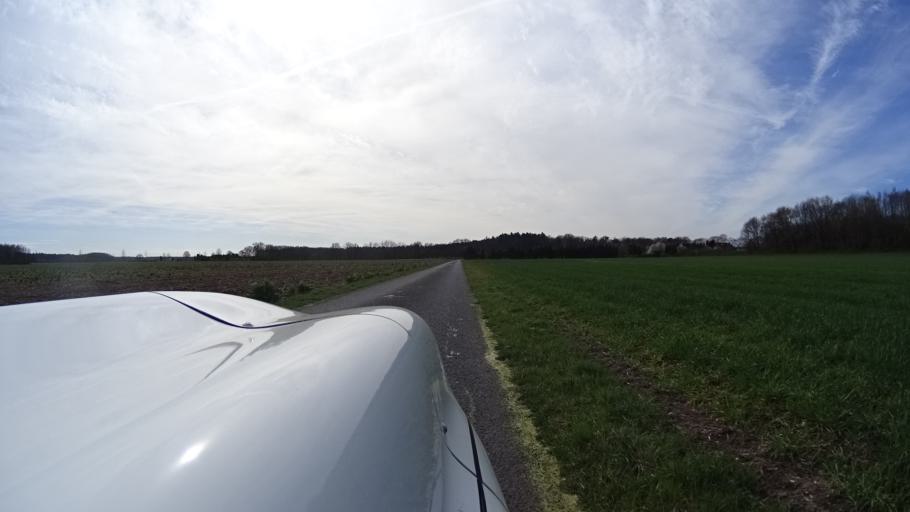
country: NL
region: Limburg
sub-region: Gemeente Venlo
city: Arcen
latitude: 51.5321
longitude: 6.2012
